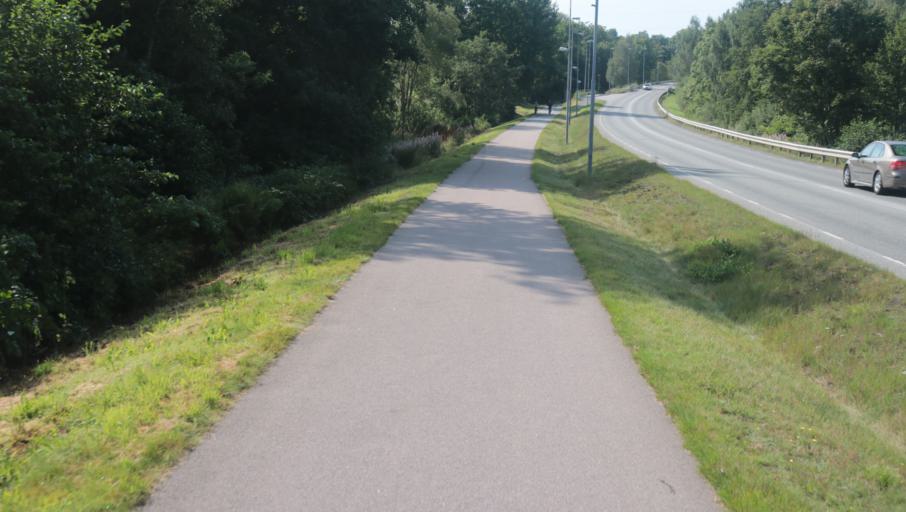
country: SE
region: Blekinge
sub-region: Karlshamns Kommun
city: Karlshamn
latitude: 56.2000
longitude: 14.8497
